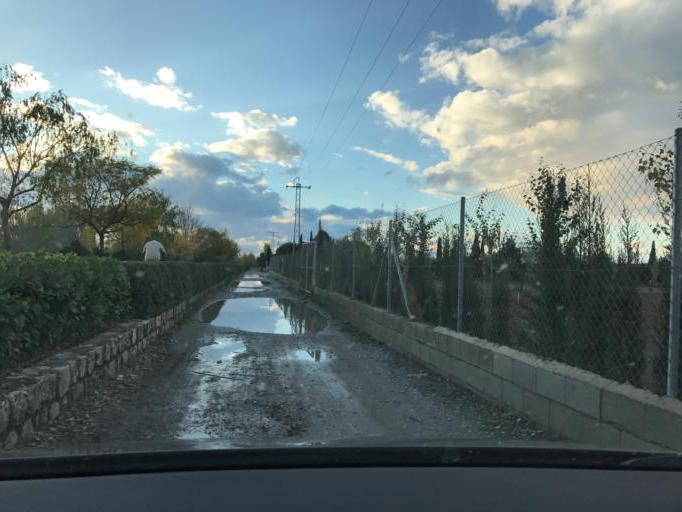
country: ES
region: Andalusia
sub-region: Provincia de Granada
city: Armilla
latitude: 37.1616
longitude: -3.6168
